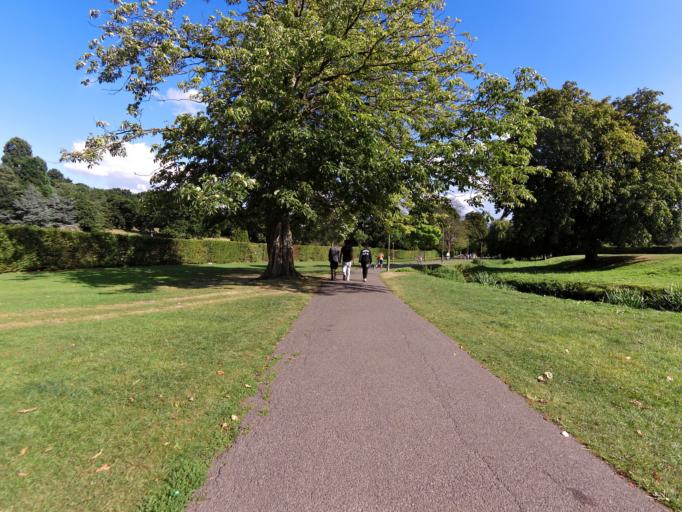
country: GB
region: England
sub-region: Greater London
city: Hadley Wood
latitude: 51.6375
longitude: -0.1529
